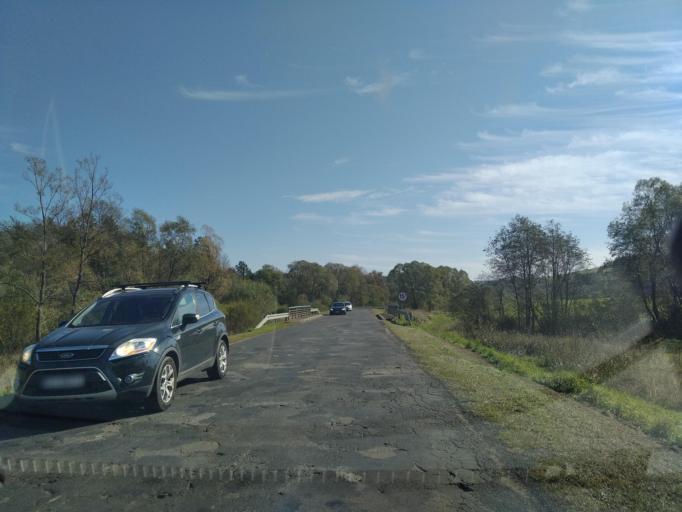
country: PL
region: Subcarpathian Voivodeship
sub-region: Powiat sanocki
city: Bukowsko
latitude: 49.4180
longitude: 21.9622
